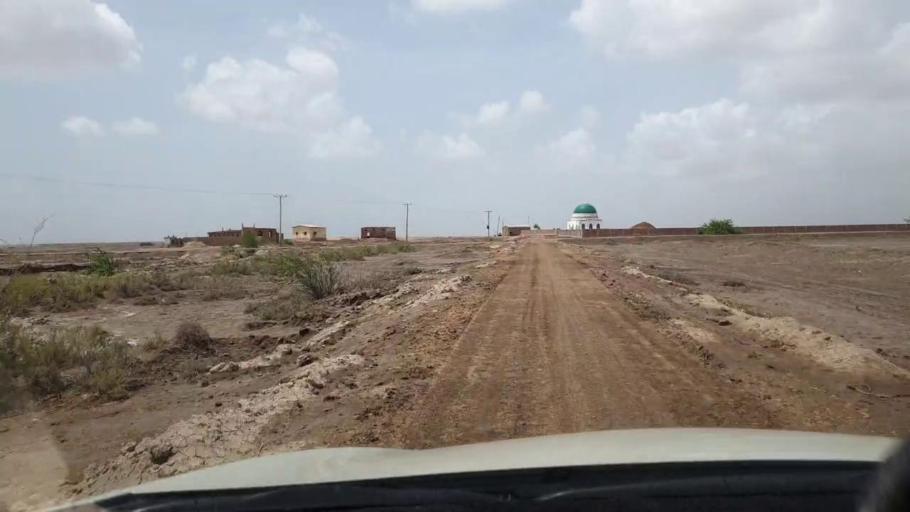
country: PK
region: Sindh
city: Kadhan
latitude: 24.3617
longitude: 68.8472
